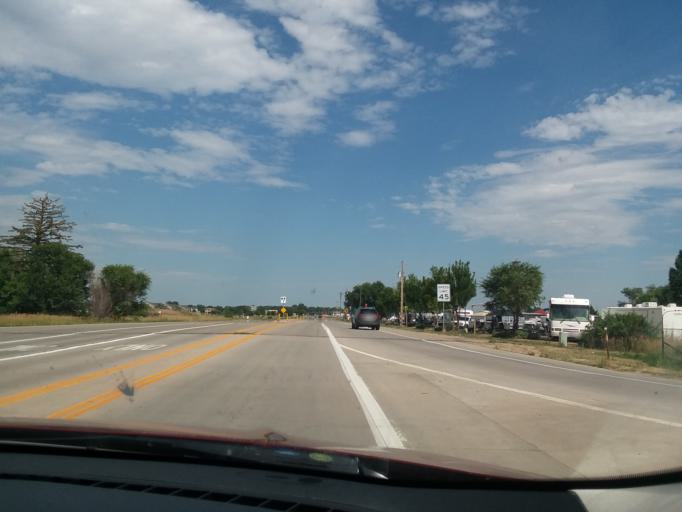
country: US
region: Colorado
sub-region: Larimer County
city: Berthoud
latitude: 40.3051
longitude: -105.1058
